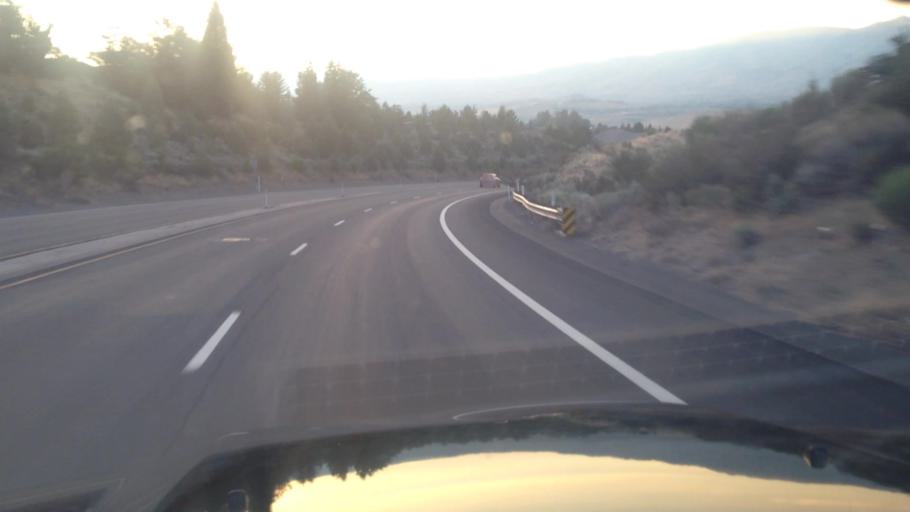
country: US
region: Nevada
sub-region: Washoe County
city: Reno
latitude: 39.4867
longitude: -119.8628
